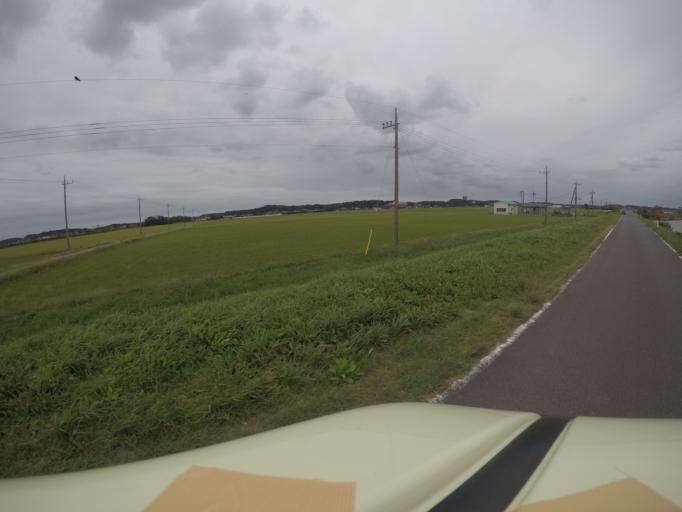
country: JP
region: Ibaraki
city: Inashiki
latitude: 36.0313
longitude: 140.3148
